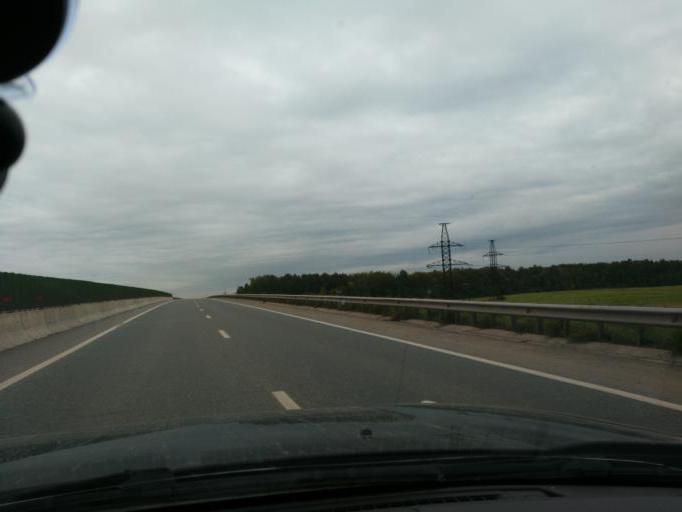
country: RU
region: Perm
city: Froly
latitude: 57.9316
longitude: 56.2892
